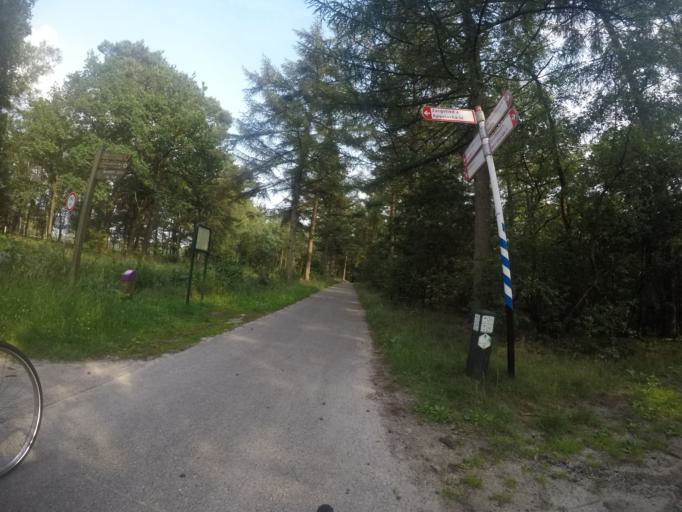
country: NL
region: Friesland
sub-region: Gemeente Weststellingwerf
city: Noordwolde
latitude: 52.8923
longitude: 6.2389
